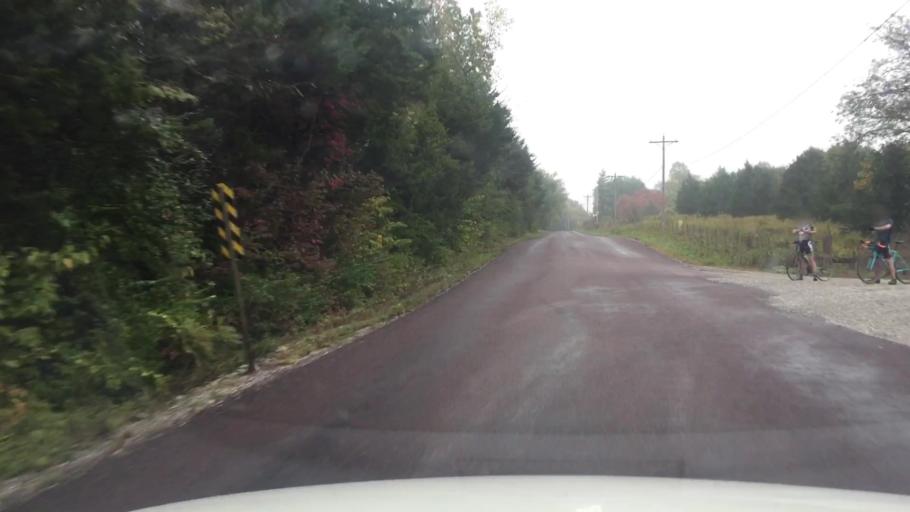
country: US
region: Missouri
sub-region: Boone County
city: Columbia
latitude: 38.8559
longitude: -92.3544
